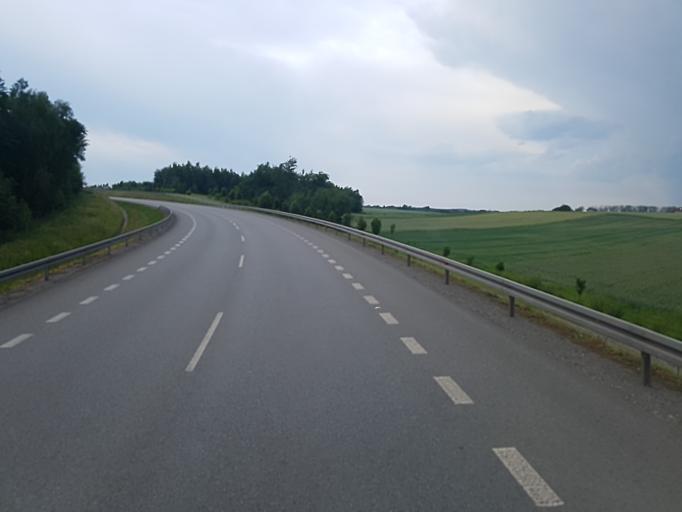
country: PL
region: Silesian Voivodeship
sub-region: Powiat pszczynski
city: Krzyzowice
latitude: 49.9732
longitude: 18.6286
